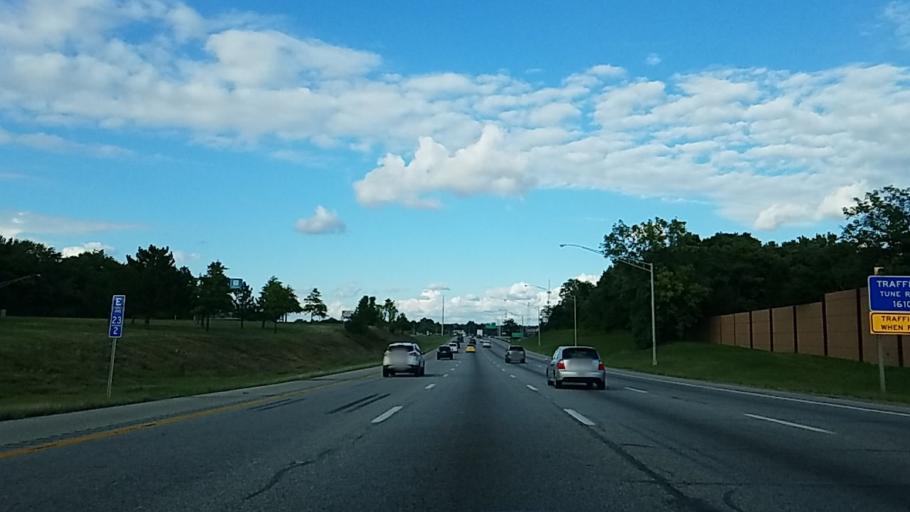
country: US
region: Ohio
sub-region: Cuyahoga County
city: Garfield Heights
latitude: 41.4193
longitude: -81.5898
